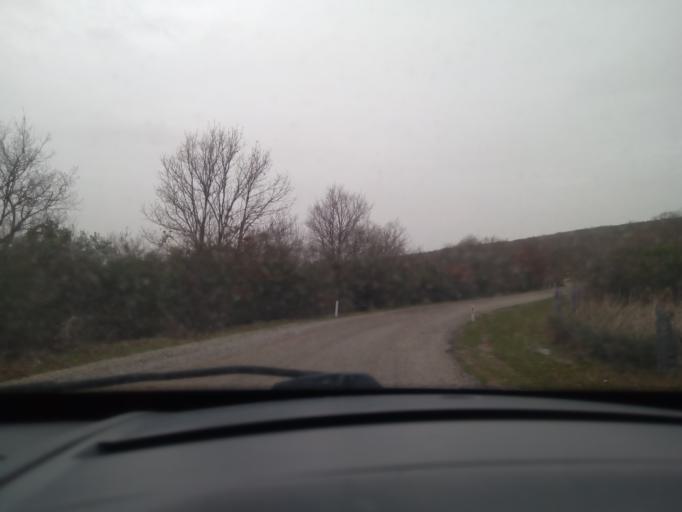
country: TR
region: Balikesir
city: Omerkoy
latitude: 39.9197
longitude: 28.0605
